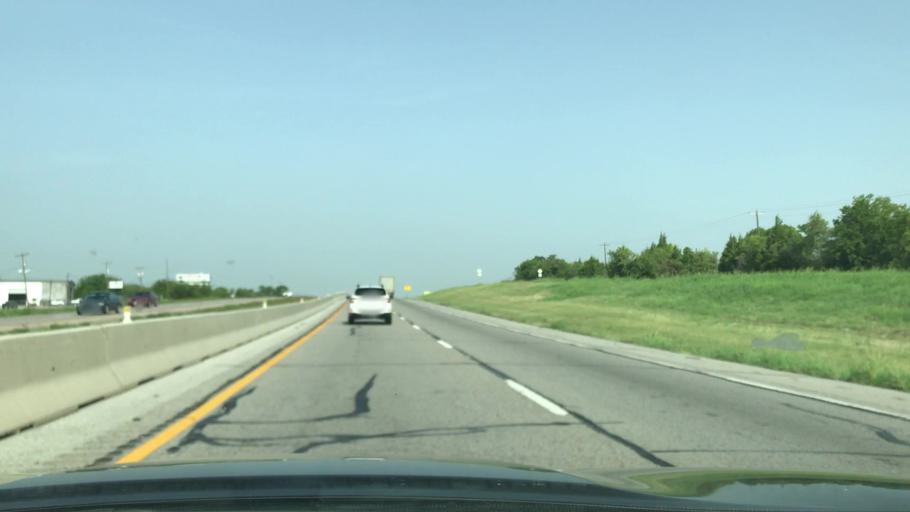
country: US
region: Texas
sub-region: Dallas County
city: Sunnyvale
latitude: 32.7791
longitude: -96.5268
